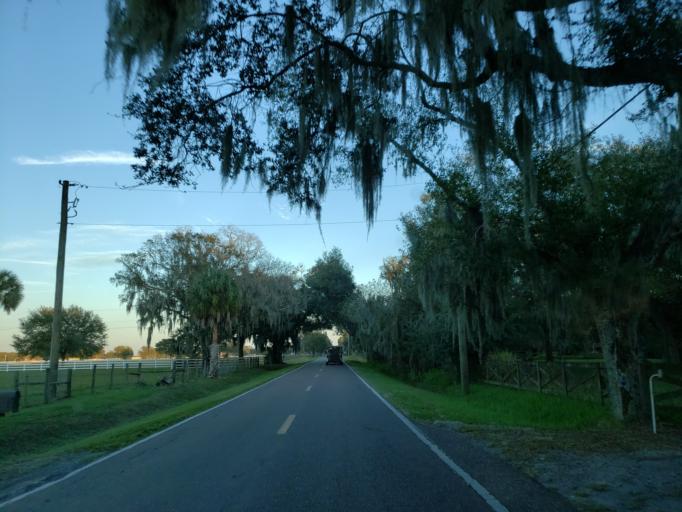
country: US
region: Florida
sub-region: Hillsborough County
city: Fish Hawk
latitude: 27.8286
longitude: -82.1845
